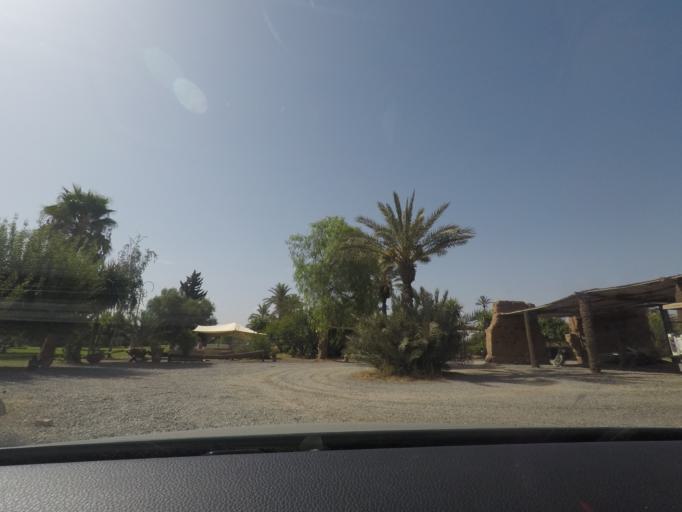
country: MA
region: Marrakech-Tensift-Al Haouz
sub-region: Marrakech
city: Marrakesh
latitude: 31.5815
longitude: -8.0250
